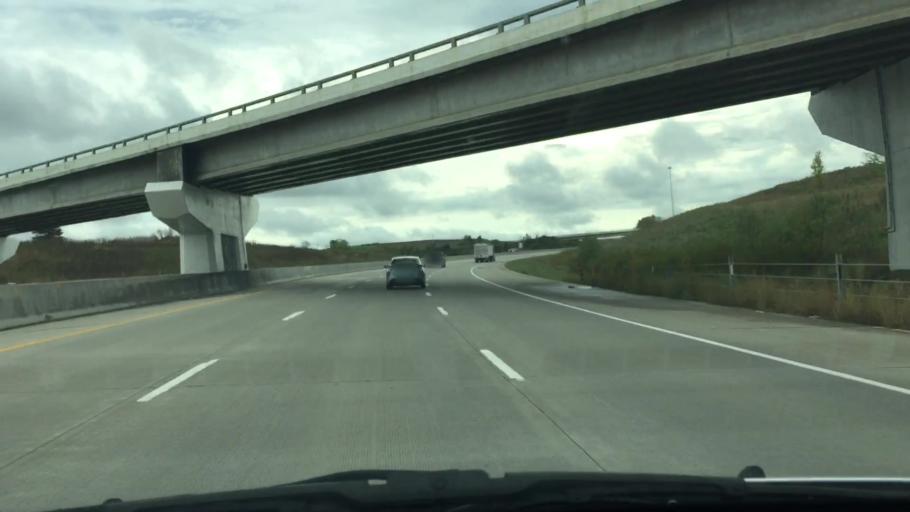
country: US
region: Iowa
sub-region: Polk County
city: West Des Moines
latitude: 41.5242
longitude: -93.7731
